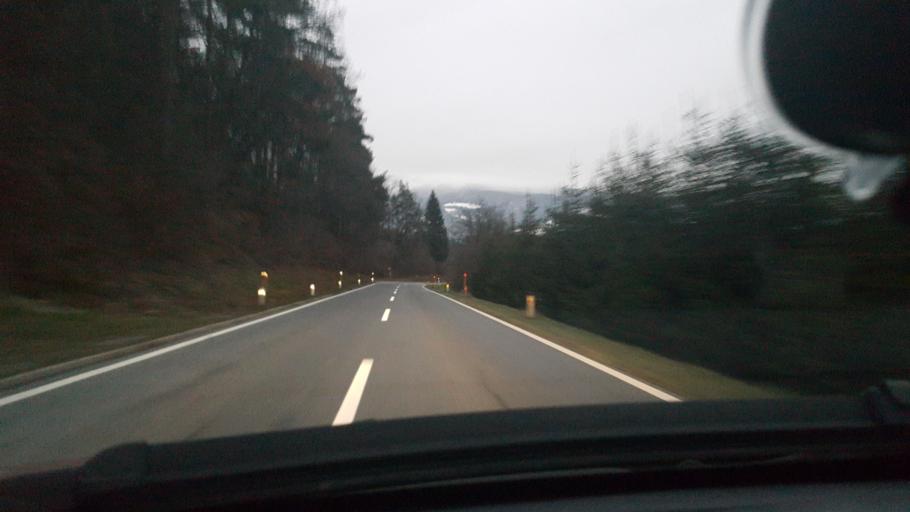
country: AT
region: Carinthia
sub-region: Politischer Bezirk Volkermarkt
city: Neuhaus
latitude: 46.6537
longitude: 14.9072
